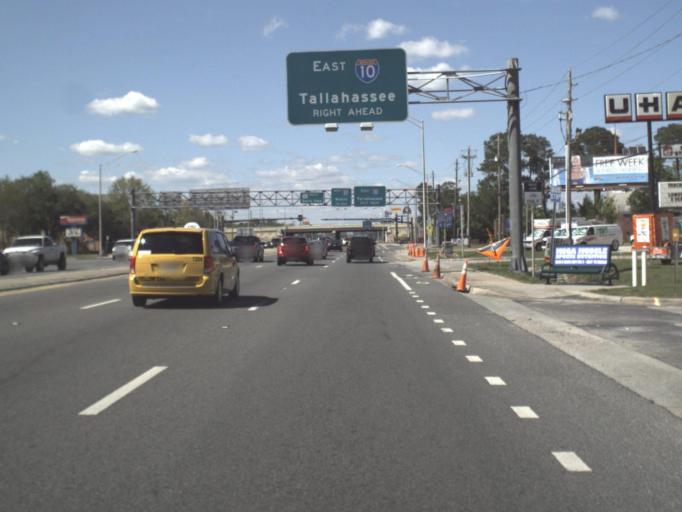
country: US
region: Florida
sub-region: Escambia County
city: Ferry Pass
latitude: 30.4998
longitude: -87.2216
